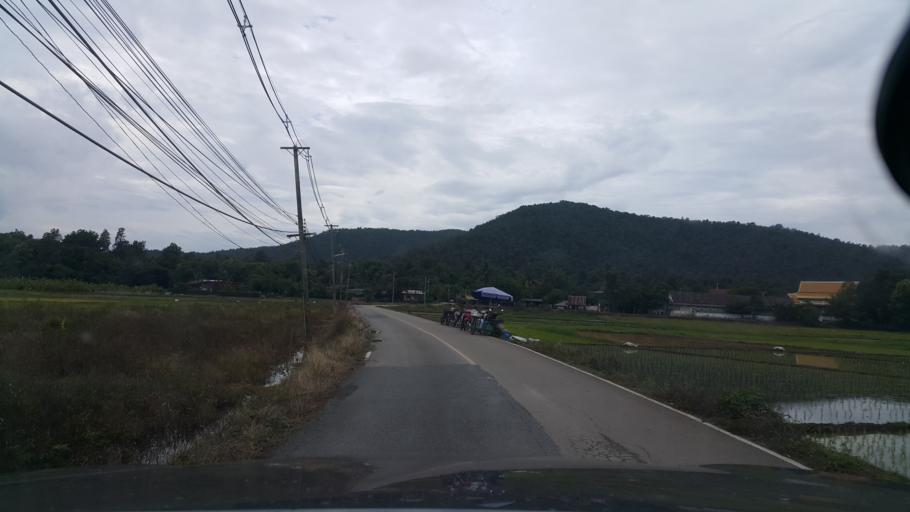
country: TH
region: Chiang Mai
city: Mae On
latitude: 18.8316
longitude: 99.1838
